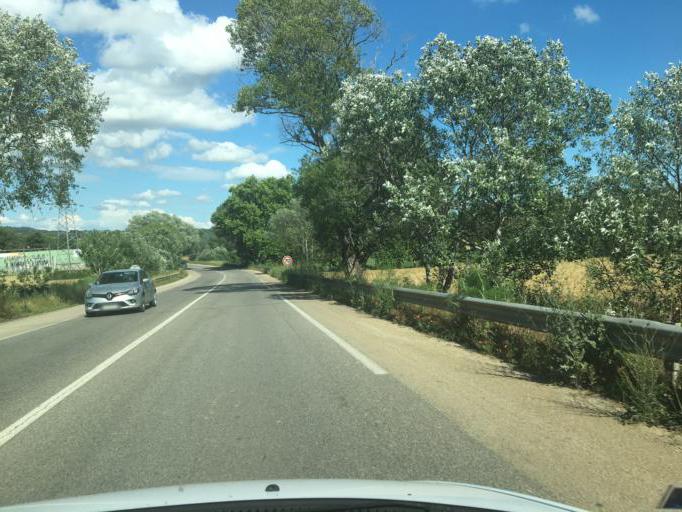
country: FR
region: Provence-Alpes-Cote d'Azur
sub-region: Departement des Bouches-du-Rhone
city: Eguilles
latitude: 43.5438
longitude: 5.3525
